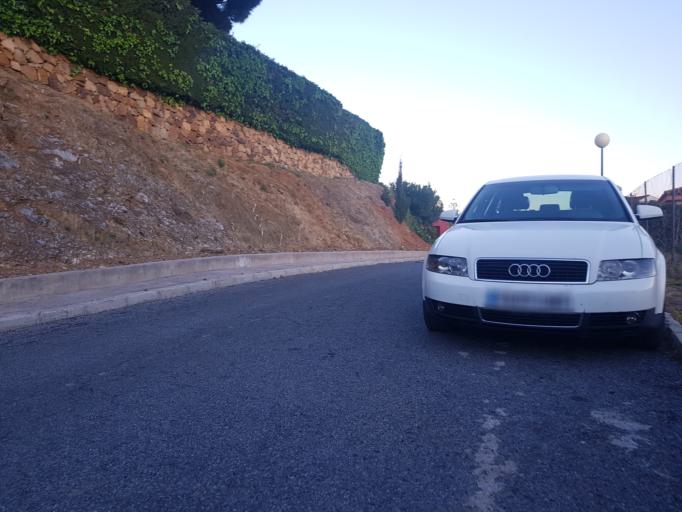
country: ES
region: Andalusia
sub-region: Provincia de Malaga
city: Marbella
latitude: 36.5218
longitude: -4.8876
